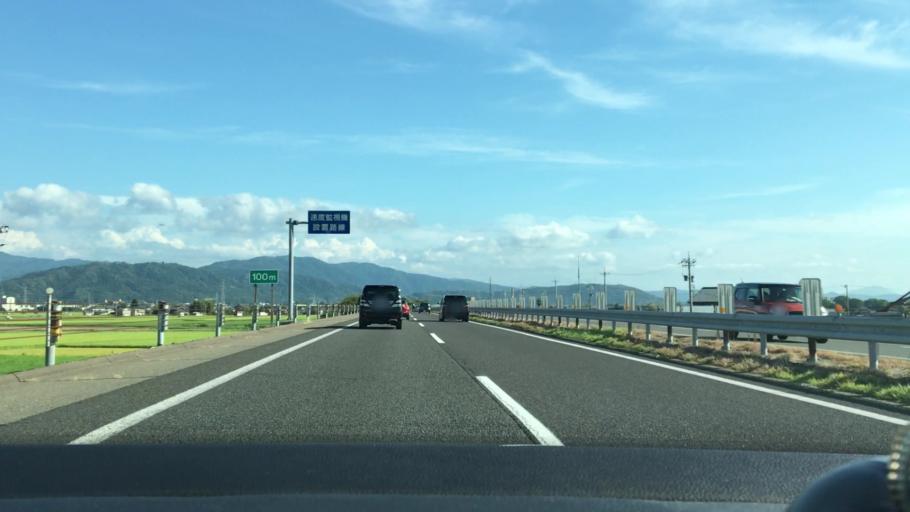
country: JP
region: Fukui
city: Maruoka
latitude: 36.1230
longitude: 136.2795
